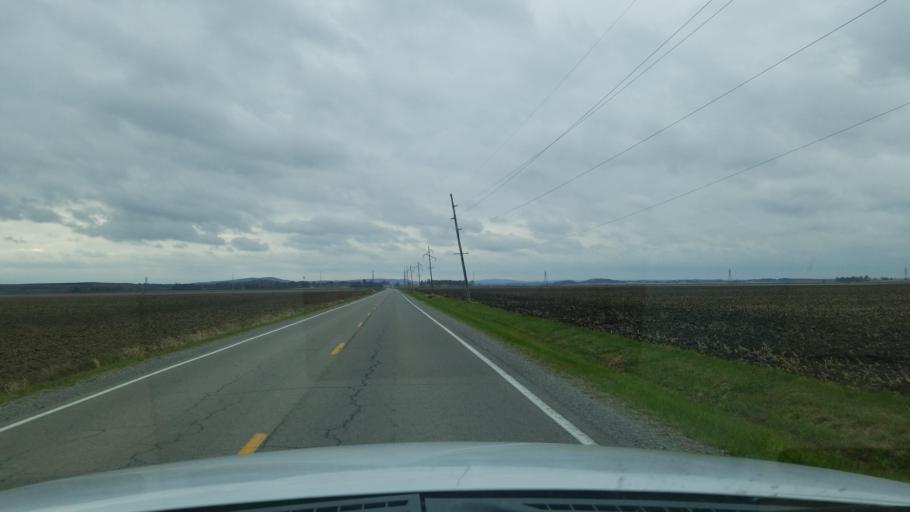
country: US
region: Illinois
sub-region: Saline County
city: Eldorado
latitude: 37.7820
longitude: -88.4382
